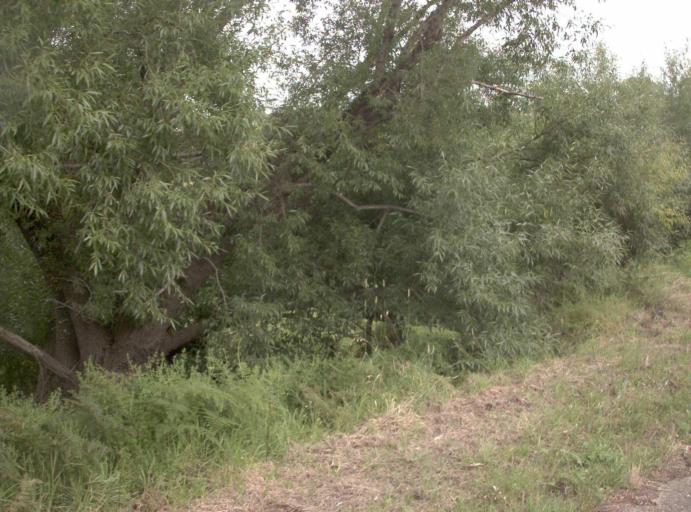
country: AU
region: Victoria
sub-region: East Gippsland
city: Bairnsdale
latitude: -37.8100
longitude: 147.6191
